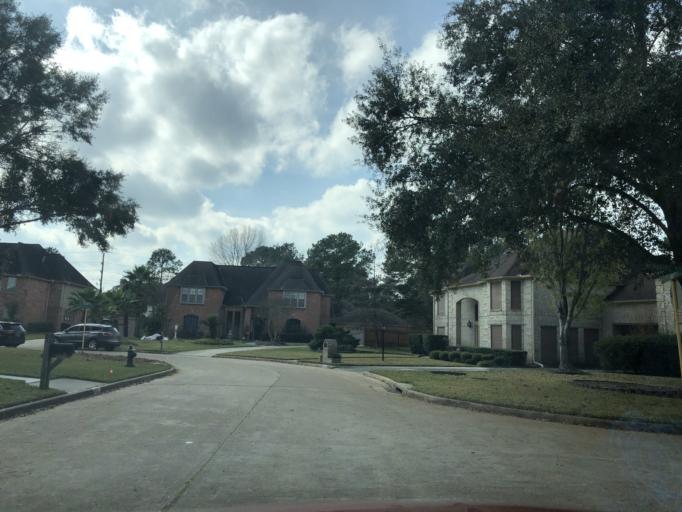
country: US
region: Texas
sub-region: Harris County
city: Tomball
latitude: 30.0257
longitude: -95.5436
